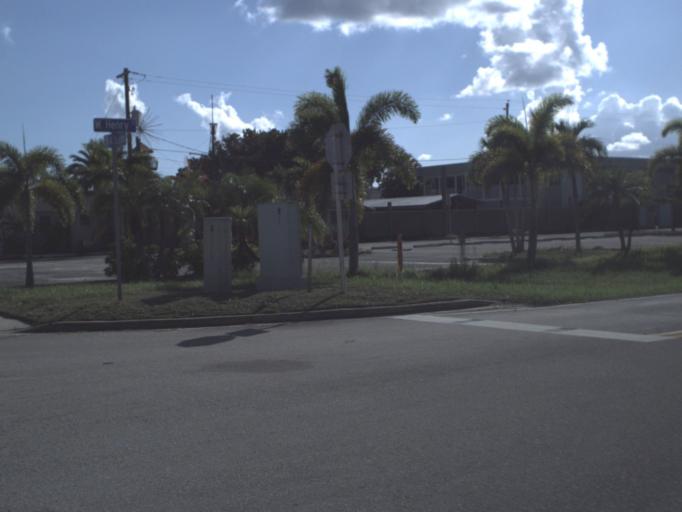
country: US
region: Florida
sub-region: Charlotte County
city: Punta Gorda
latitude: 26.9243
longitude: -82.0474
